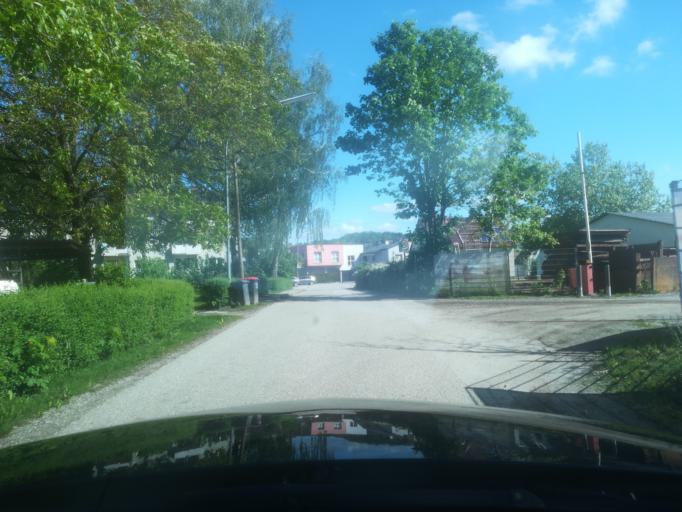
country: AT
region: Upper Austria
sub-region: Politischer Bezirk Perg
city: Perg
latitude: 48.2456
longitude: 14.6248
